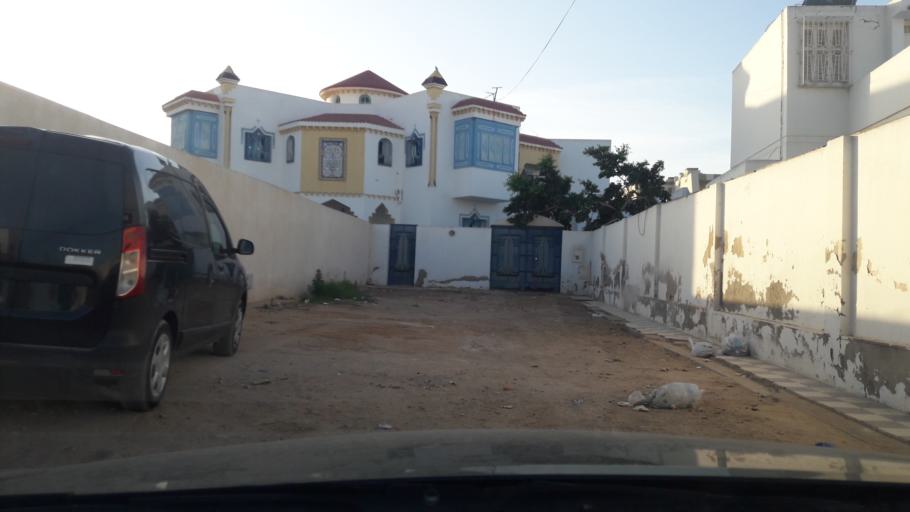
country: TN
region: Safaqis
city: Al Qarmadah
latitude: 34.7956
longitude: 10.7516
